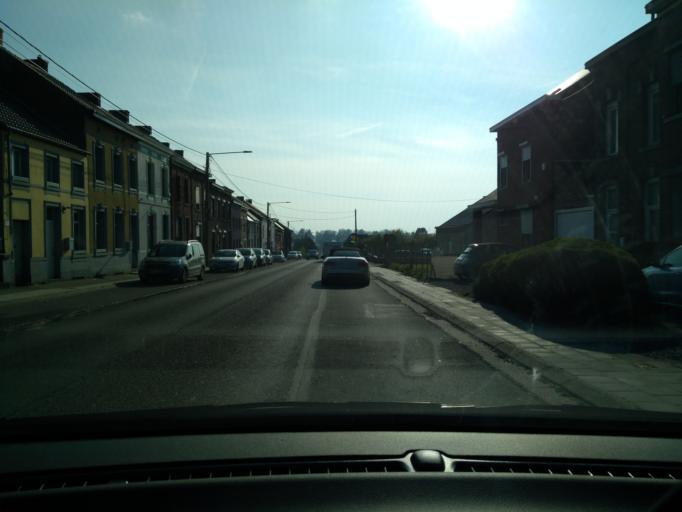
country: BE
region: Wallonia
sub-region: Province du Hainaut
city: Morlanwelz-Mariemont
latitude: 50.4534
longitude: 4.2518
